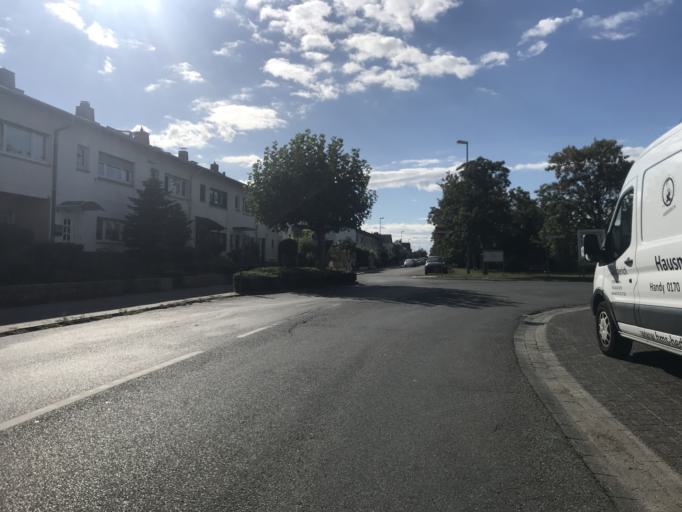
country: DE
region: Hesse
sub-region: Regierungsbezirk Darmstadt
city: Hochheim am Main
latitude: 50.0100
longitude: 8.3613
